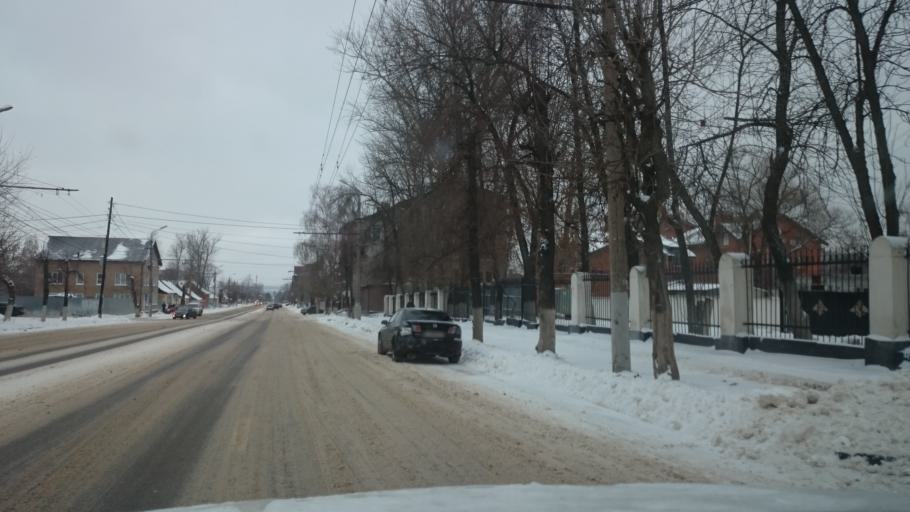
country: RU
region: Tula
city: Mendeleyevskiy
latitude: 54.1772
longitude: 37.5742
